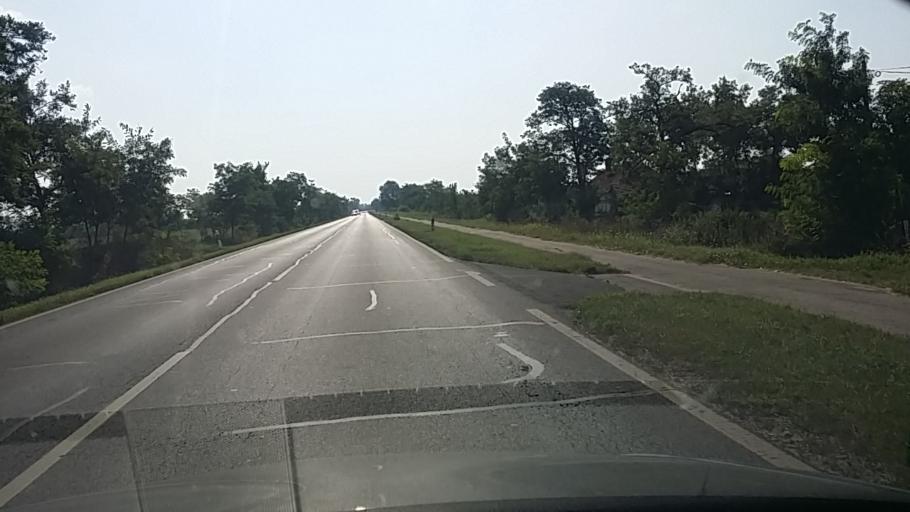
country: HU
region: Bekes
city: Kondoros
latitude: 46.7424
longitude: 20.8734
